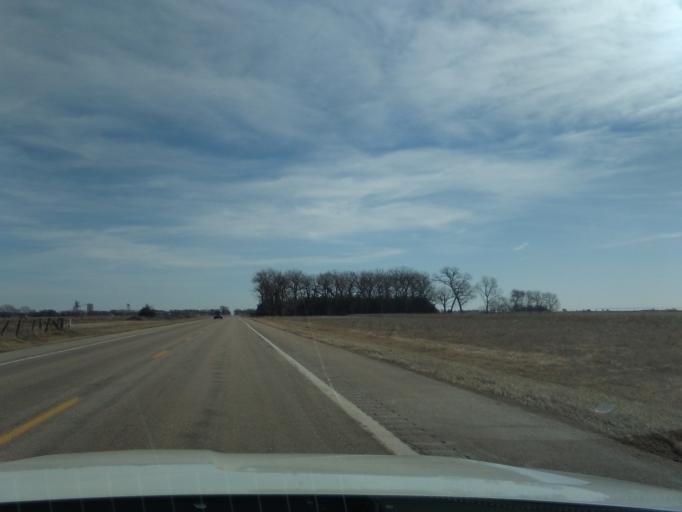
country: US
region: Nebraska
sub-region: Fillmore County
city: Geneva
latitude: 40.6404
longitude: -97.4769
